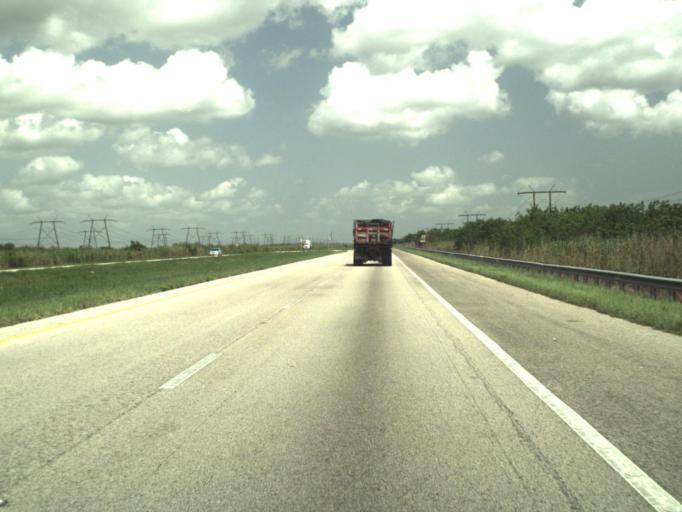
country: US
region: Florida
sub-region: Broward County
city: Weston
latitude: 26.2621
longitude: -80.4815
